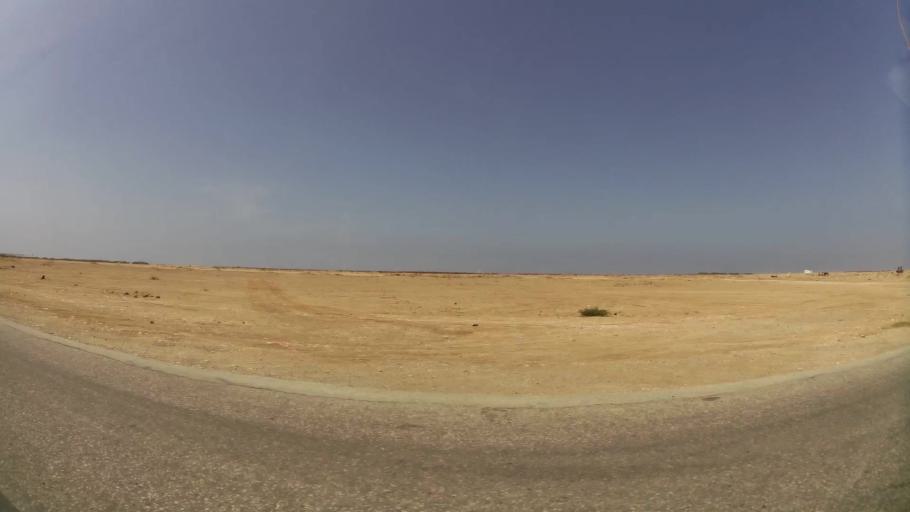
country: OM
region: Zufar
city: Salalah
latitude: 17.0379
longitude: 54.2751
